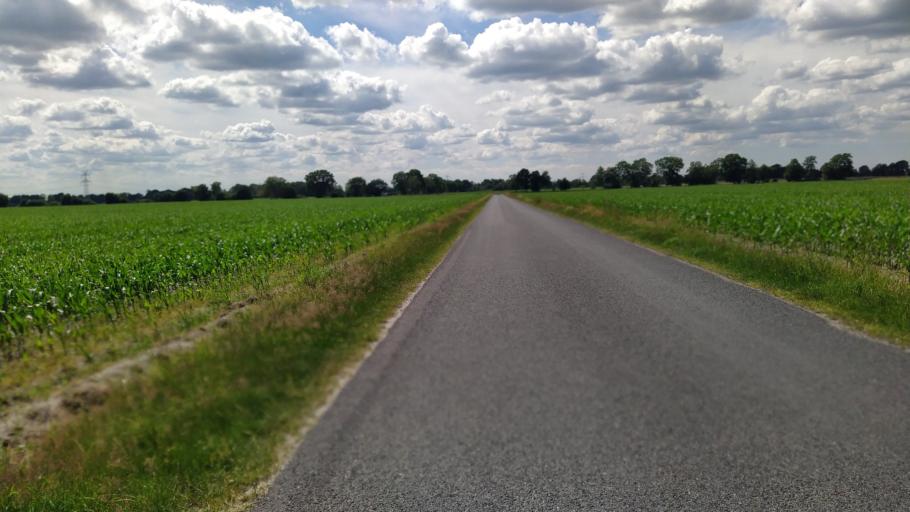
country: DE
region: Lower Saxony
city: Hollnseth
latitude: 53.5736
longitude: 9.1422
